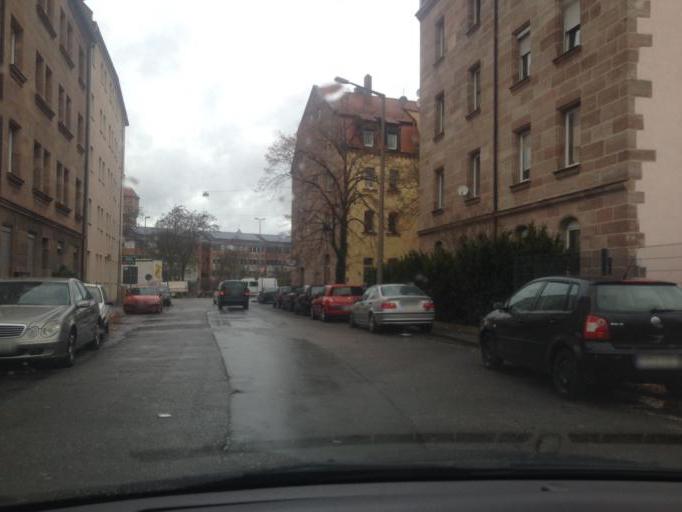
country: DE
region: Bavaria
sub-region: Regierungsbezirk Mittelfranken
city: Nuernberg
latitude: 49.4350
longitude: 11.0612
